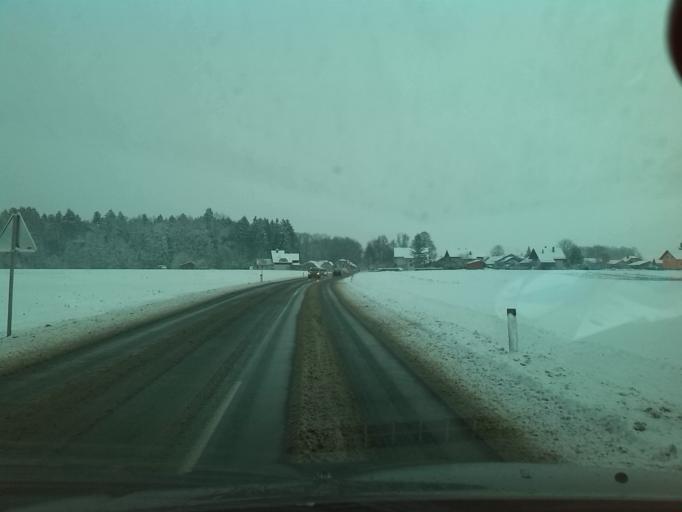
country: SI
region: Komenda
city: Komenda
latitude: 46.1941
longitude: 14.5322
